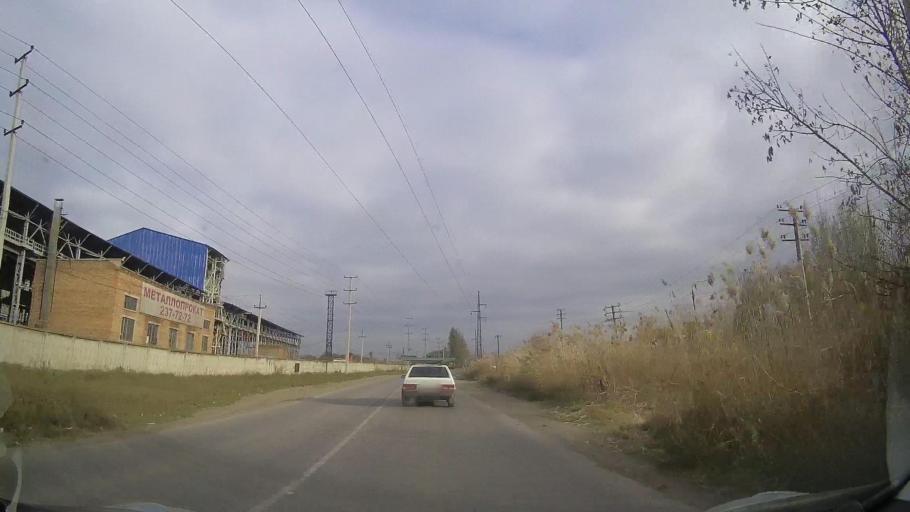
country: RU
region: Rostov
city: Bataysk
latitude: 47.1139
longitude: 39.7671
